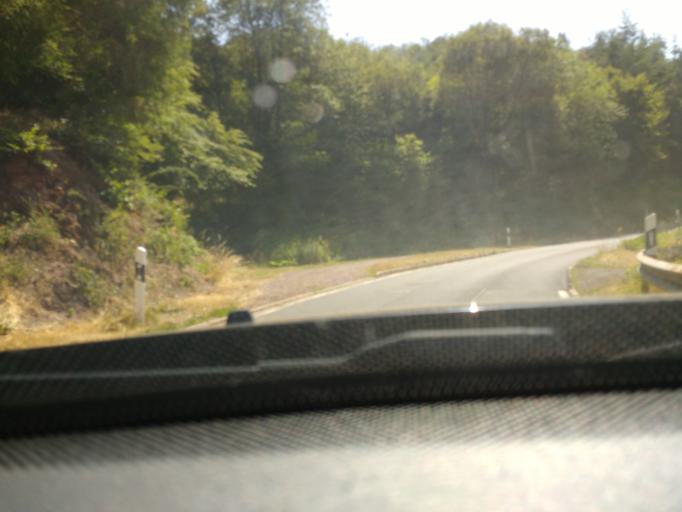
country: DE
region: Rheinland-Pfalz
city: Meerfeld
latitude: 50.0883
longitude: 6.7538
